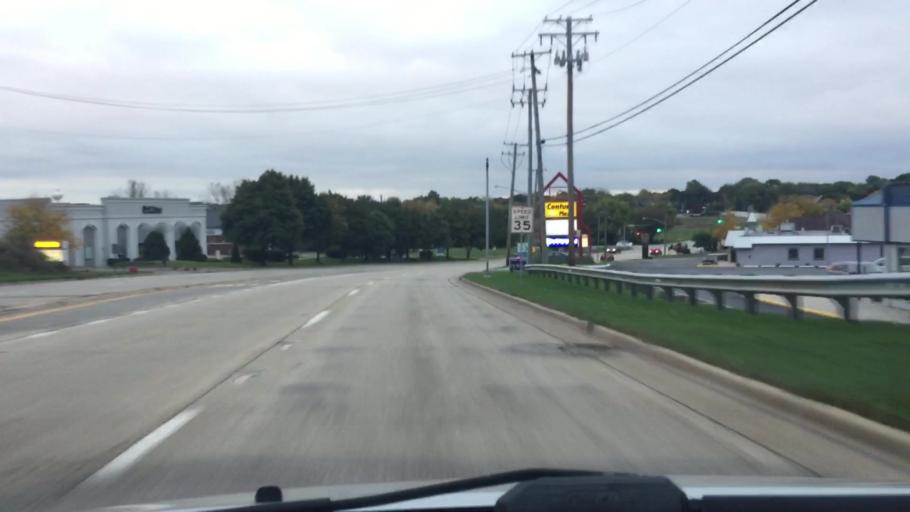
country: US
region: Illinois
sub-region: Kane County
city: West Dundee
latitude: 42.0888
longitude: -88.2896
